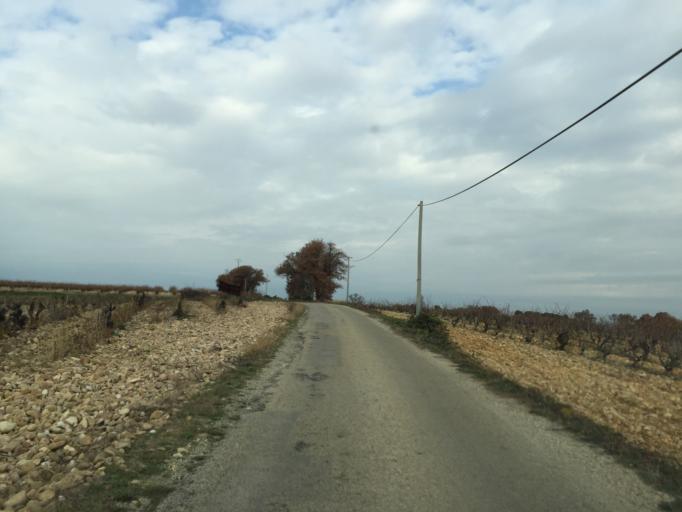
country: FR
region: Provence-Alpes-Cote d'Azur
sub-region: Departement du Vaucluse
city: Bedarrides
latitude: 44.0490
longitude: 4.8724
